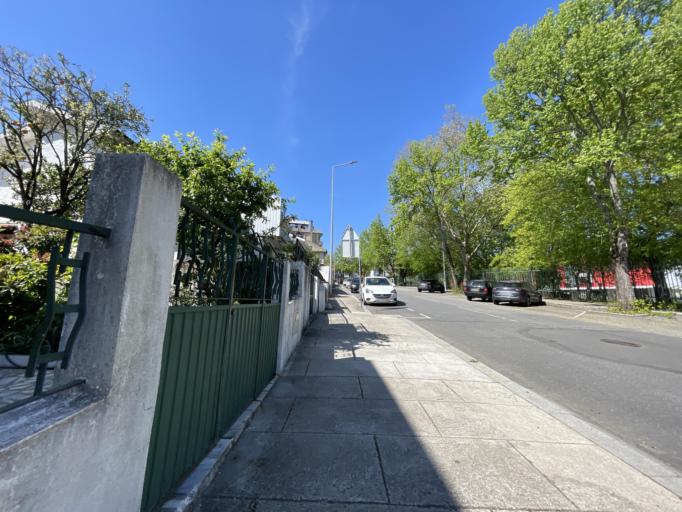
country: PT
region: Braga
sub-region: Guimaraes
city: Guimaraes
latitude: 41.4445
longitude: -8.2843
